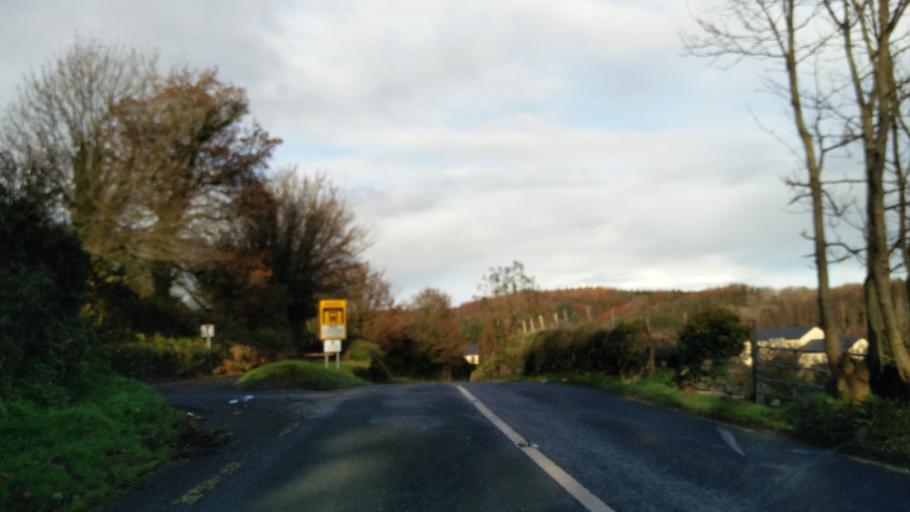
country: IE
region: Connaught
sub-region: Maigh Eo
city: Westport
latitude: 53.7915
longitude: -9.5040
